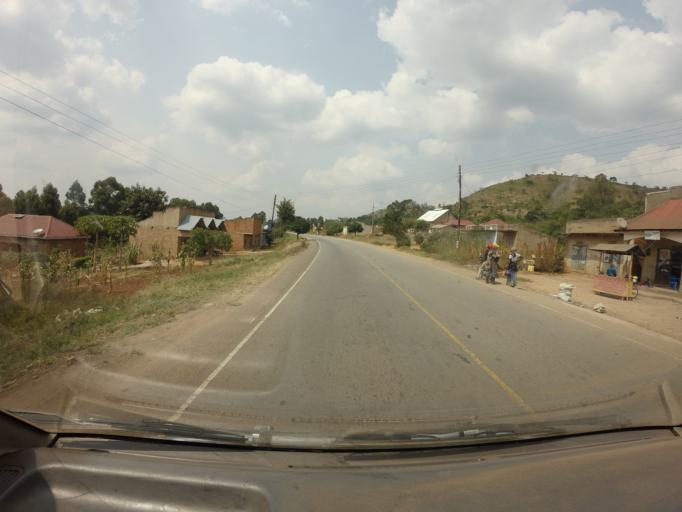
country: UG
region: Central Region
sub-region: Lyantonde District
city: Lyantonde
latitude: -0.3916
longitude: 31.1848
